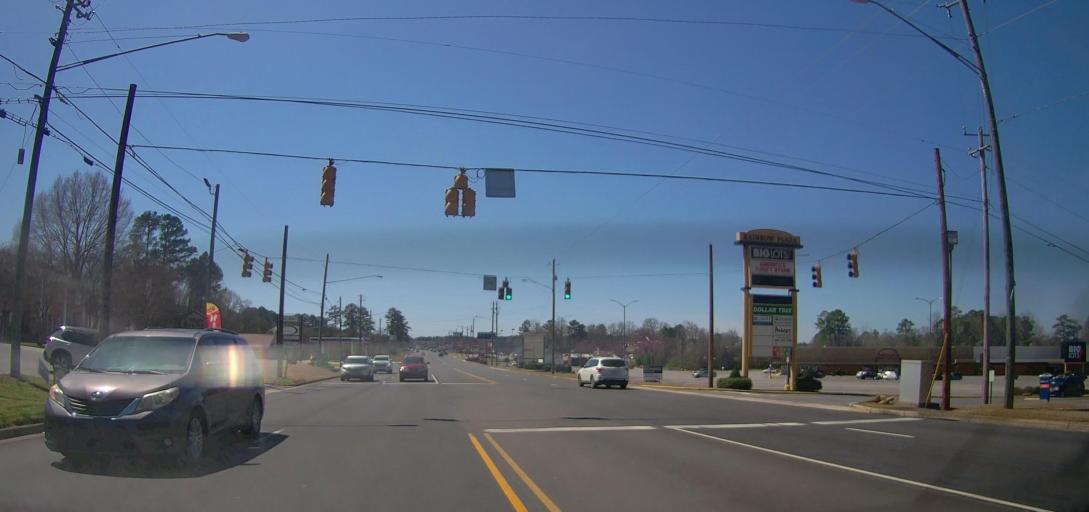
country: US
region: Alabama
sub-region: Etowah County
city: Rainbow City
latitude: 33.9611
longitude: -86.0333
